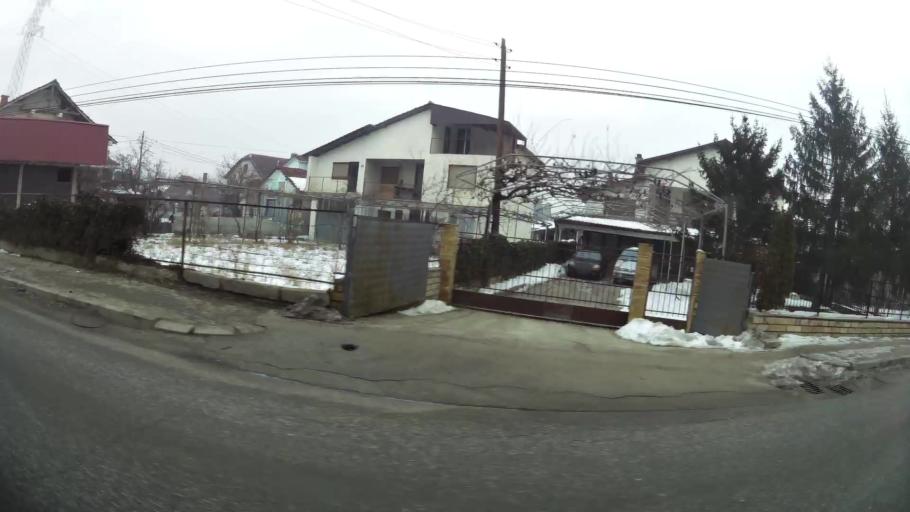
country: MK
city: Kondovo
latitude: 42.0395
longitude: 21.3480
